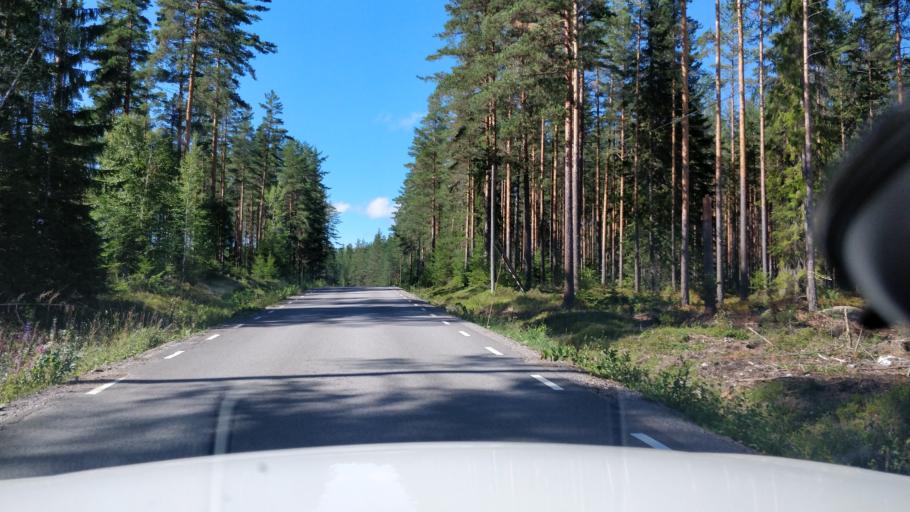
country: SE
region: Dalarna
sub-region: Faluns Kommun
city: Bjursas
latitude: 60.7505
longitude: 15.5256
